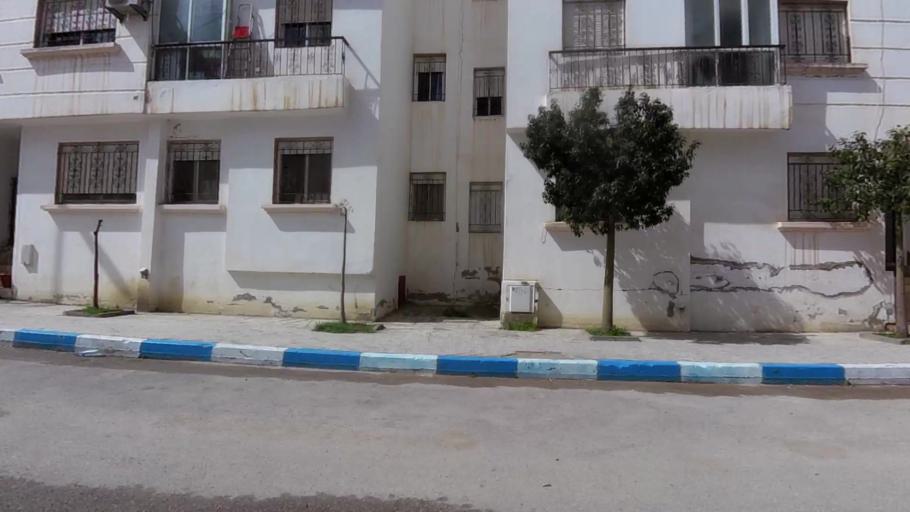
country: MA
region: Tanger-Tetouan
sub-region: Tanger-Assilah
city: Tangier
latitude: 35.7671
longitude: -5.7609
